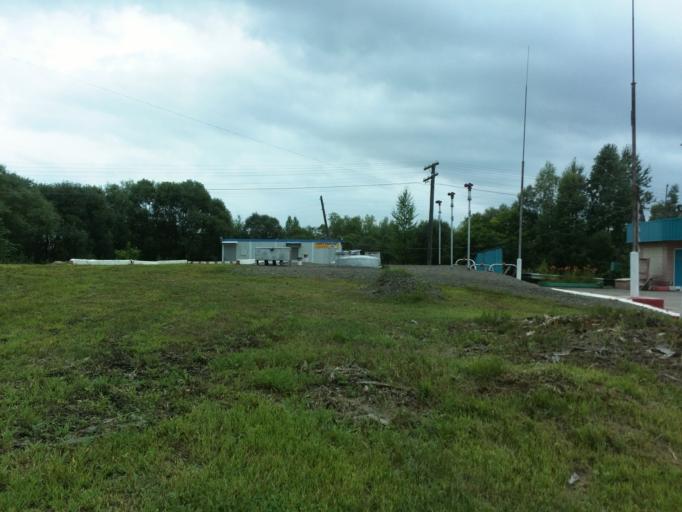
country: RU
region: Primorskiy
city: Novopokrovka
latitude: 45.8586
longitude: 134.5219
